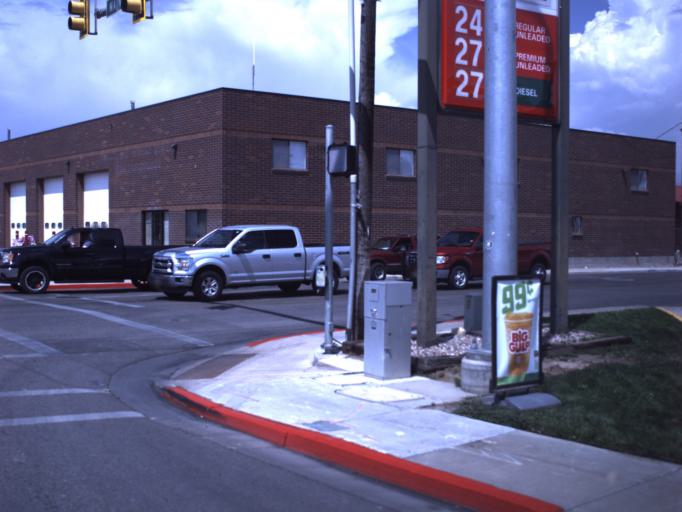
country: US
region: Utah
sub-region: Uintah County
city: Vernal
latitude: 40.4559
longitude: -109.5188
